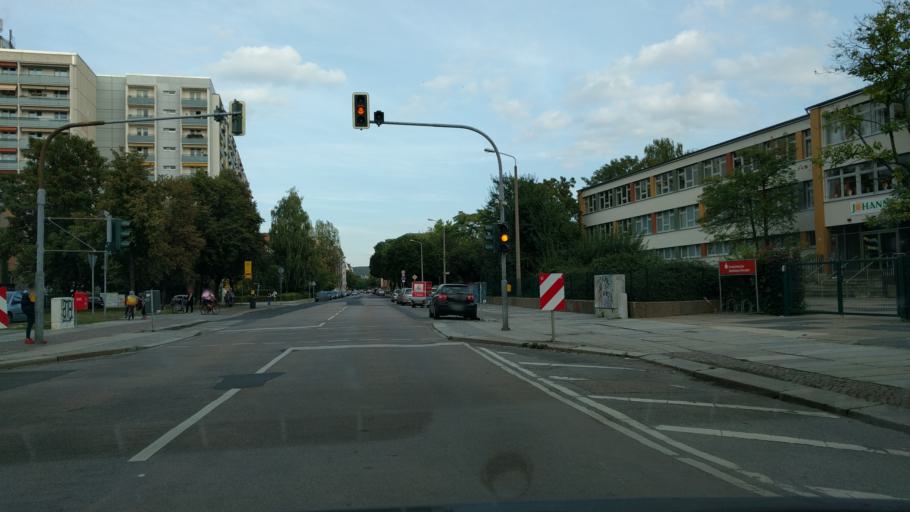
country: DE
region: Saxony
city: Albertstadt
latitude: 51.0562
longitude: 13.7653
